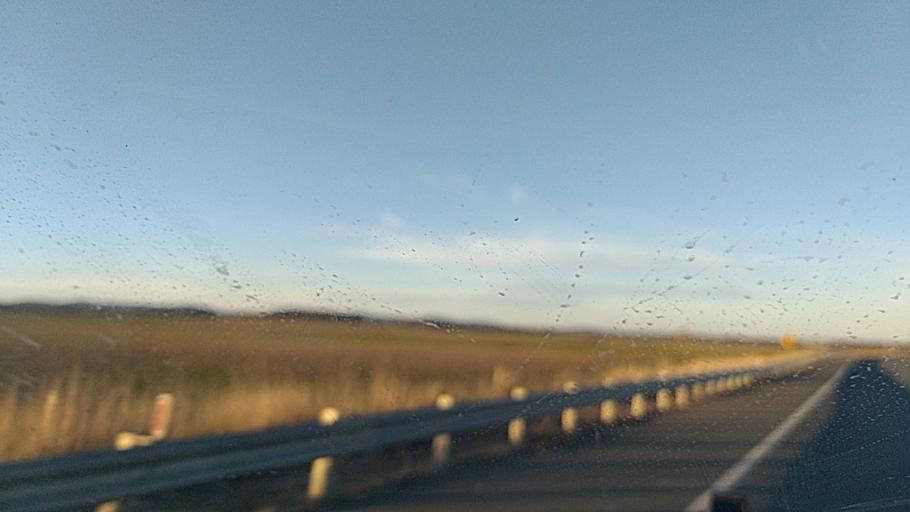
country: AU
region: New South Wales
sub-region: Goulburn Mulwaree
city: Goulburn
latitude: -34.8509
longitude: 149.5551
